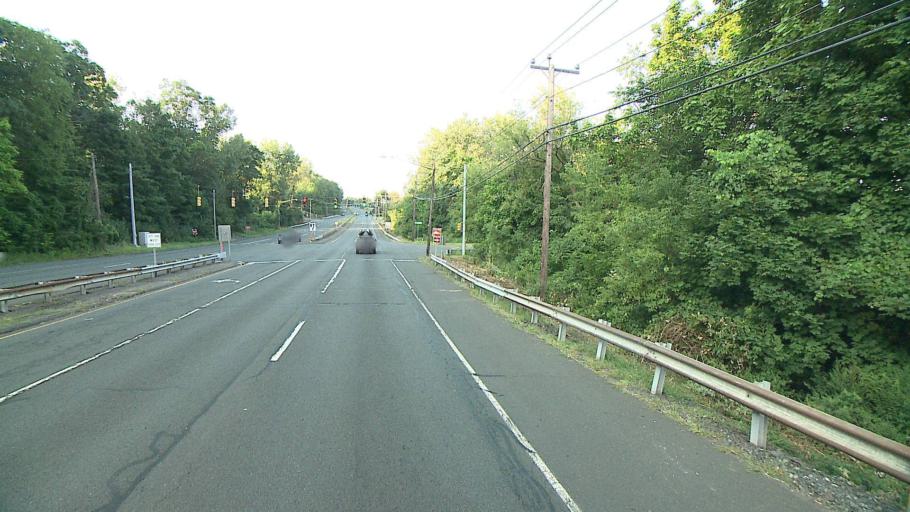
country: US
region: Connecticut
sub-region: Hartford County
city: Kensington
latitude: 41.5857
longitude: -72.7624
